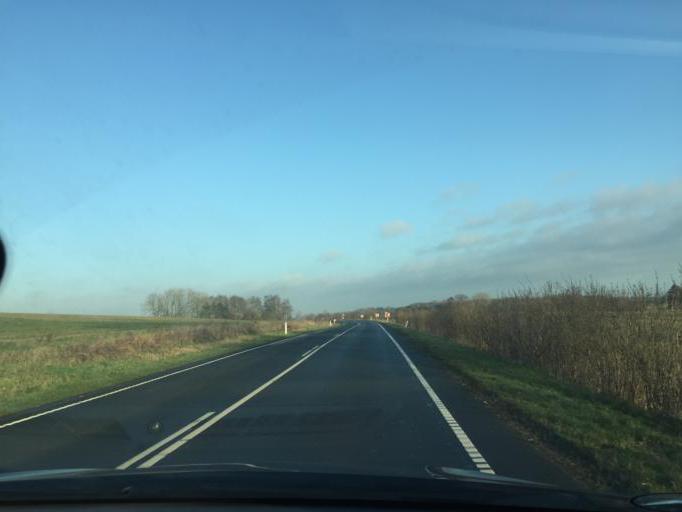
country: DK
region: South Denmark
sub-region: Faaborg-Midtfyn Kommune
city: Faaborg
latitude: 55.1718
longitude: 10.2869
